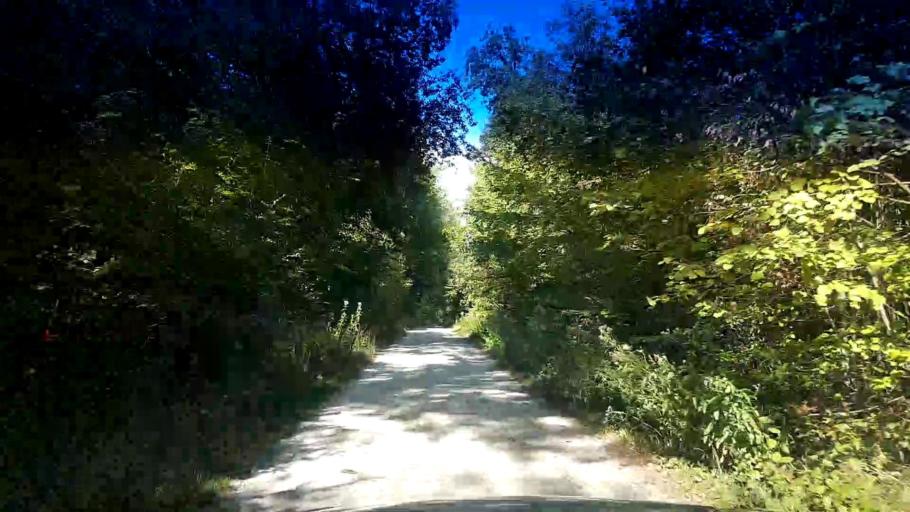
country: DE
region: Bavaria
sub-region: Upper Franconia
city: Litzendorf
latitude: 49.8913
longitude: 11.0192
